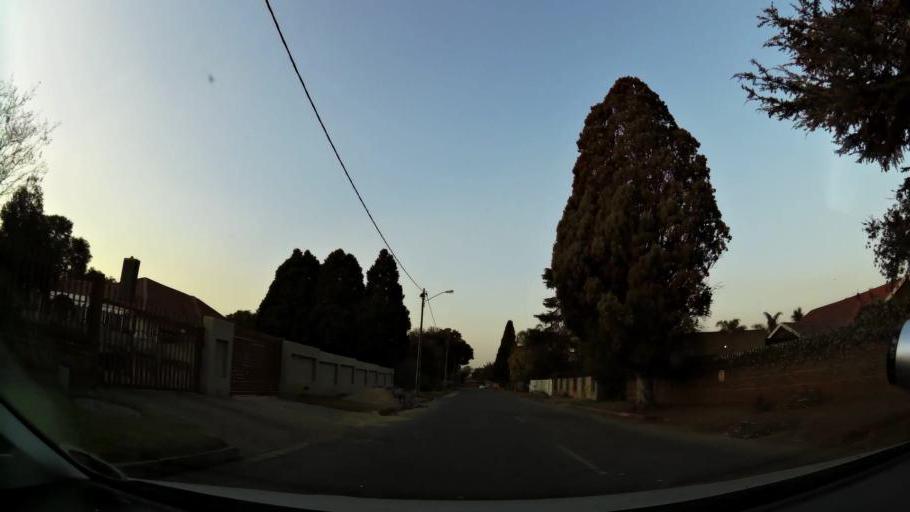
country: ZA
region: Gauteng
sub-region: Ekurhuleni Metropolitan Municipality
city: Tembisa
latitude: -26.0606
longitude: 28.2287
